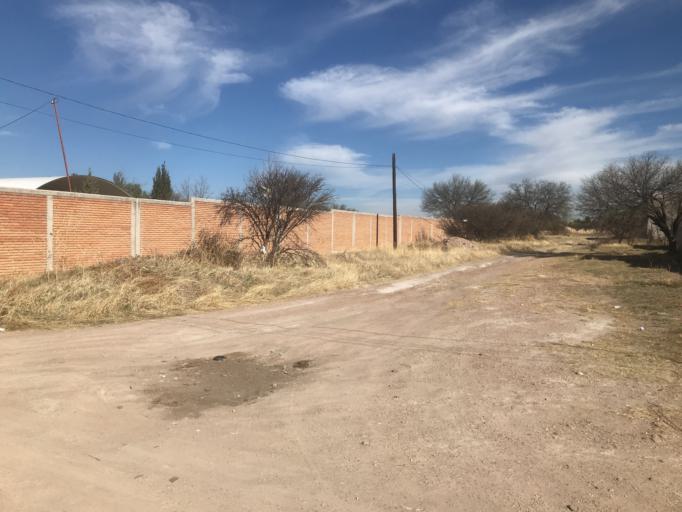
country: MX
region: Durango
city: Victoria de Durango
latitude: 24.0195
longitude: -104.5823
